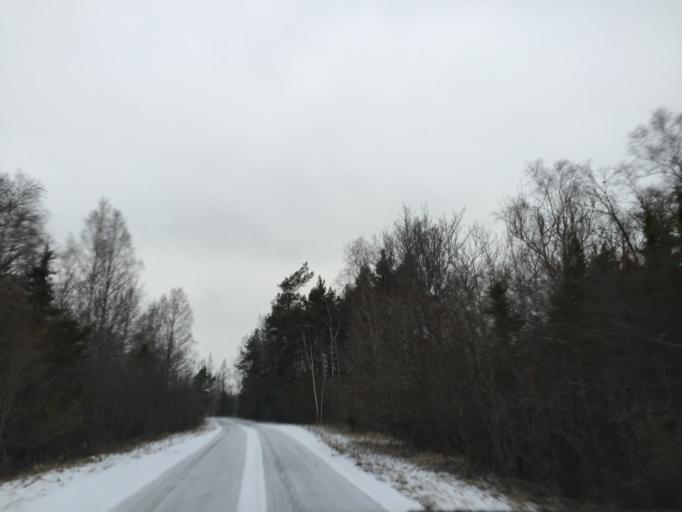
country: EE
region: Saare
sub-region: Orissaare vald
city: Orissaare
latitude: 58.6793
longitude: 23.1961
